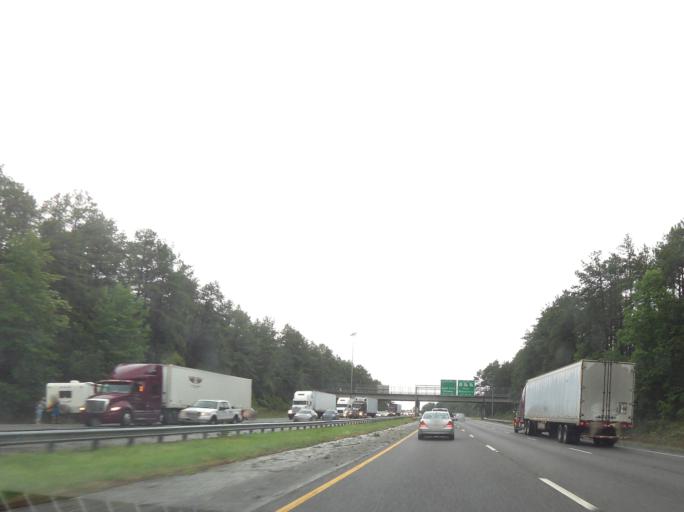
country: US
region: Georgia
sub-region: Houston County
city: Perry
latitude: 32.4565
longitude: -83.7515
